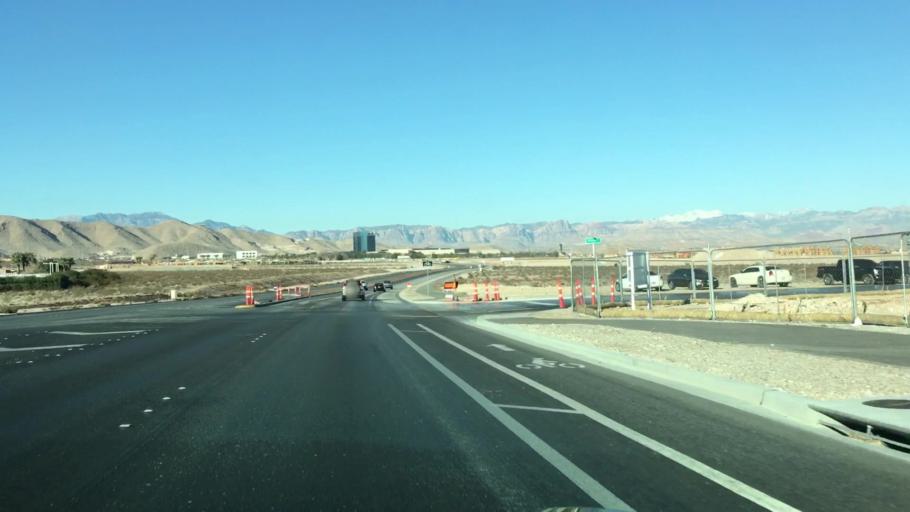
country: US
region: Nevada
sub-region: Clark County
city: Enterprise
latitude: 35.9605
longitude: -115.1499
